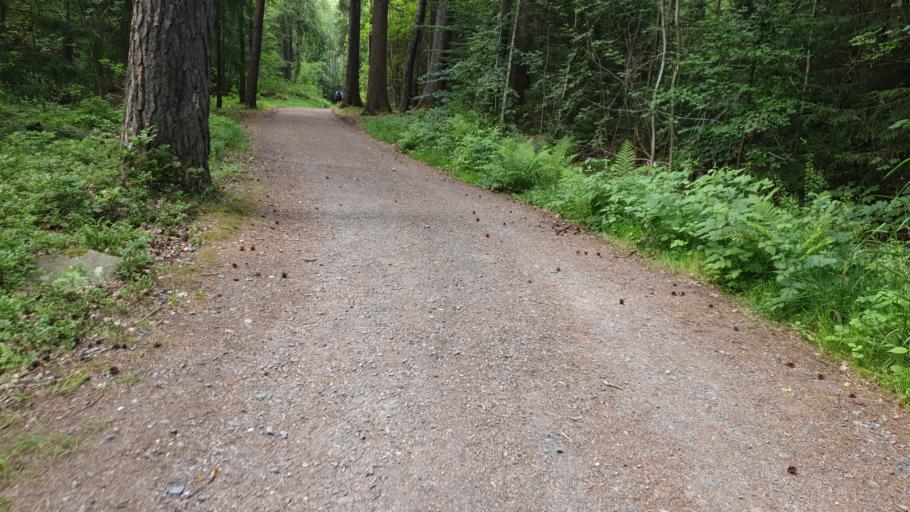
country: SE
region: Vaestra Goetaland
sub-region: Molndal
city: Moelndal
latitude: 57.6673
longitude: 12.0439
